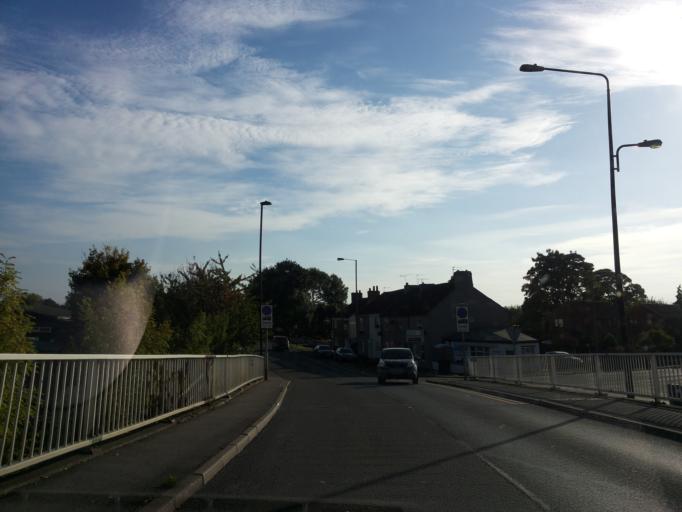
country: GB
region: England
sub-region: Doncaster
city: Hatfield
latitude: 53.6077
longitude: -0.9646
